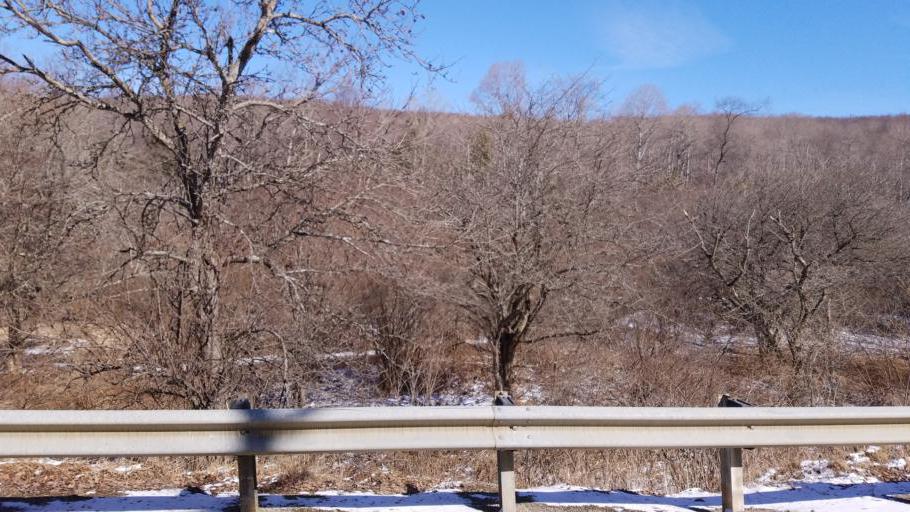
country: US
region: New York
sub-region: Allegany County
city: Andover
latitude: 41.9387
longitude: -77.8071
